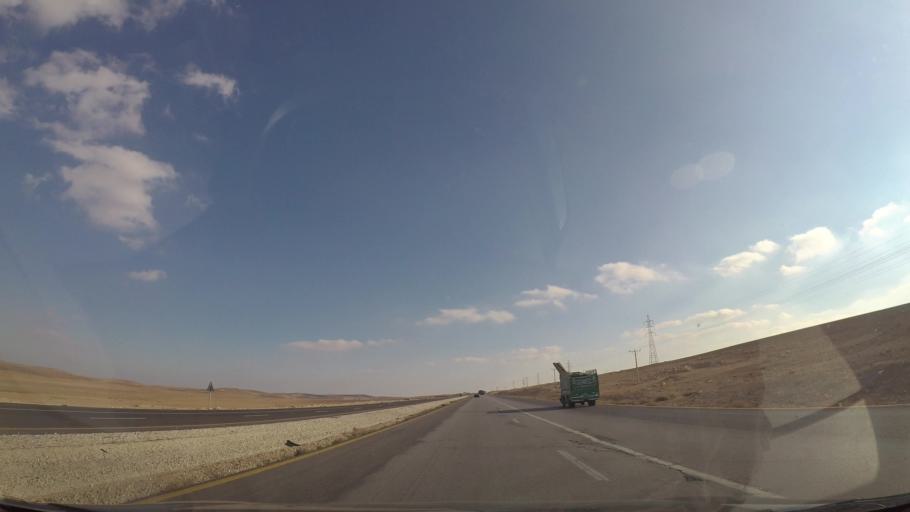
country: JO
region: Karak
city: Karak City
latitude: 31.1529
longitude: 36.0244
